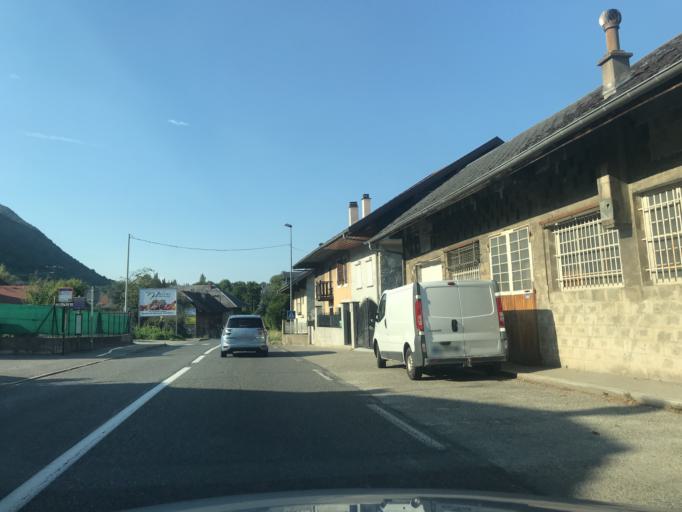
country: FR
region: Rhone-Alpes
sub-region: Departement de la Savoie
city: Gresy-sur-Aix
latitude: 45.7227
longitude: 5.9184
